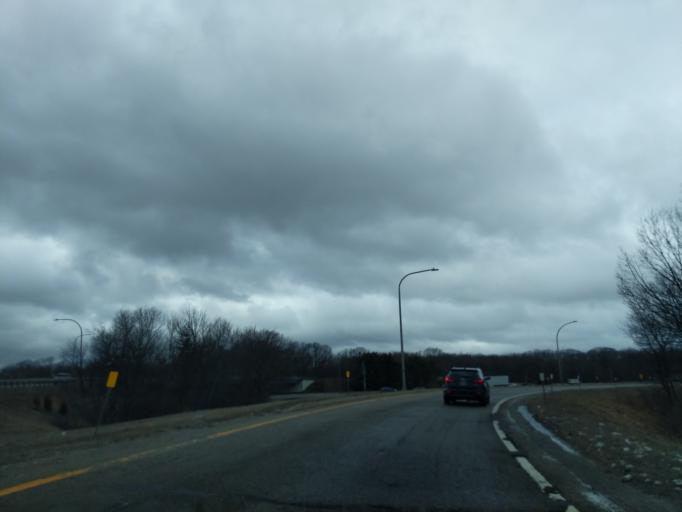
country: US
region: Rhode Island
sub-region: Kent County
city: Warwick
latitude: 41.7277
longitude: -71.4567
